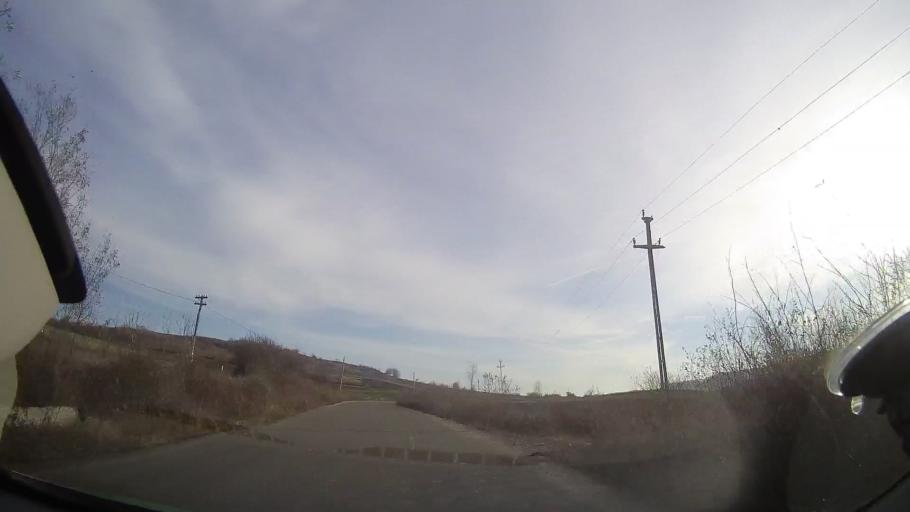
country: RO
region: Bihor
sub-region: Comuna Sarbi
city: Burzuc
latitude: 47.1653
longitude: 22.1608
